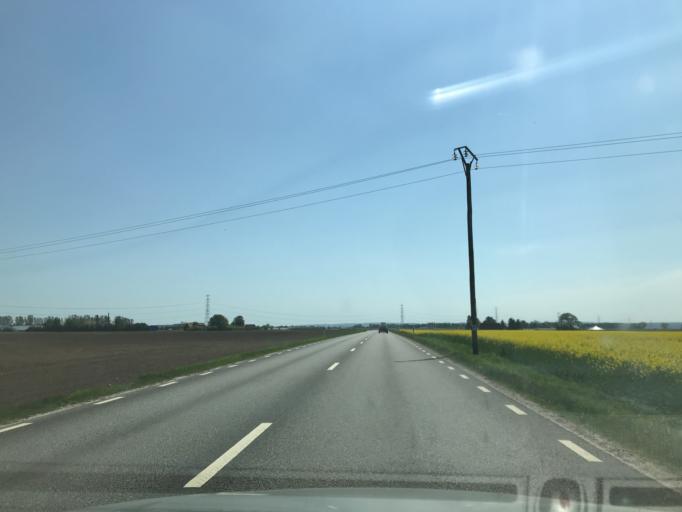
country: SE
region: Skane
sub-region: Astorps Kommun
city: Kvidinge
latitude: 56.2019
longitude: 13.0449
